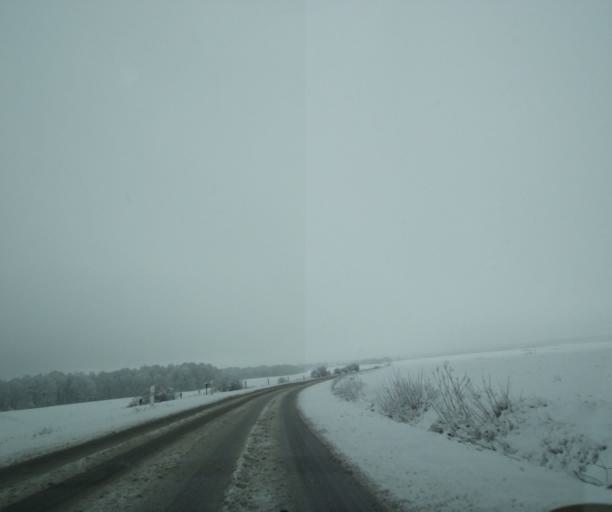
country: FR
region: Champagne-Ardenne
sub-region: Departement de la Haute-Marne
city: Saint-Dizier
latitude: 48.5989
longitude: 4.9095
